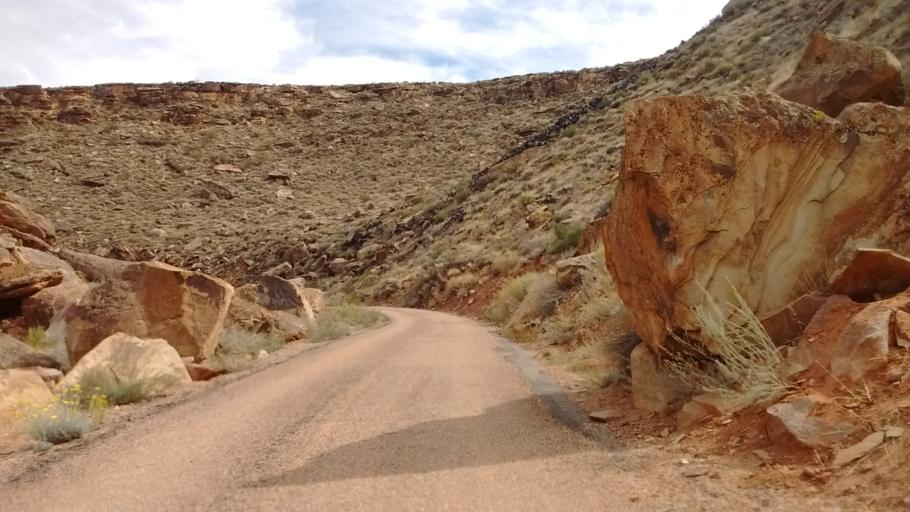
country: US
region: Utah
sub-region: Washington County
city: Washington
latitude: 37.1266
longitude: -113.4802
